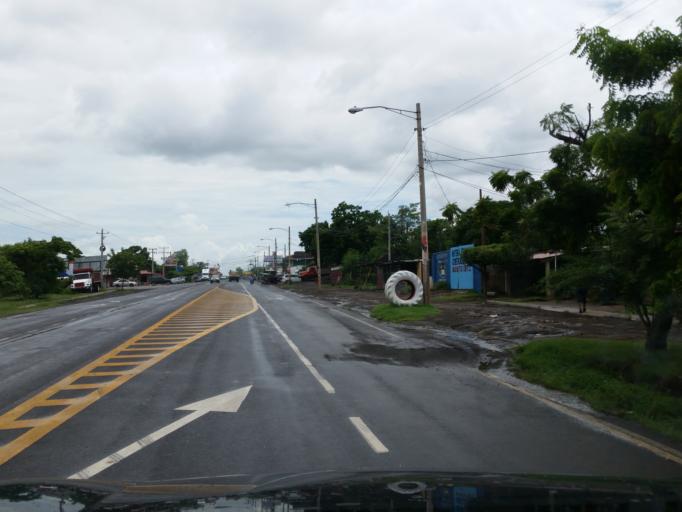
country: NI
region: Managua
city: Tipitapa
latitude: 12.3113
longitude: -86.0545
